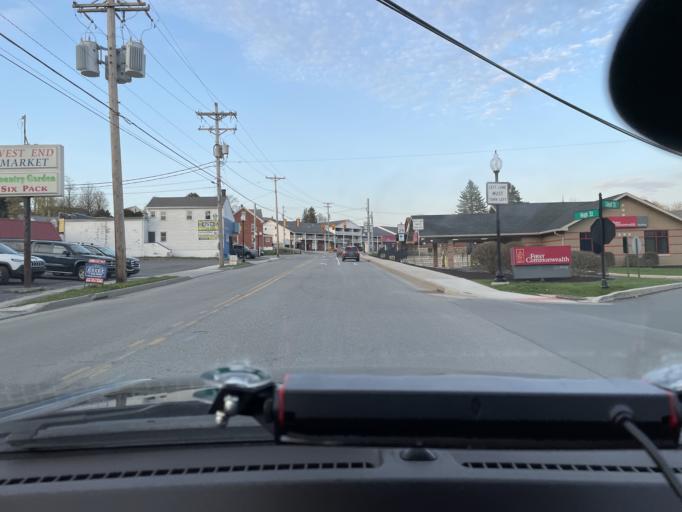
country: US
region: Pennsylvania
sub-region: Cambria County
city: Ebensburg
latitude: 40.4843
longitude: -78.7326
